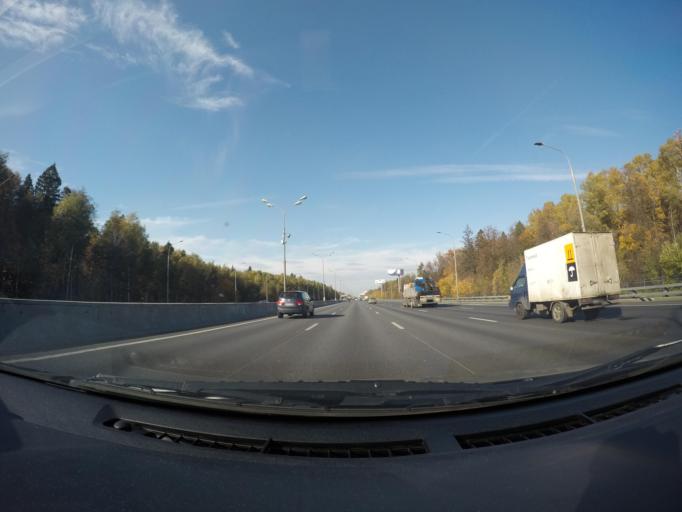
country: RU
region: Moscow
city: Gol'yanovo
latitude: 55.8431
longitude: 37.8026
